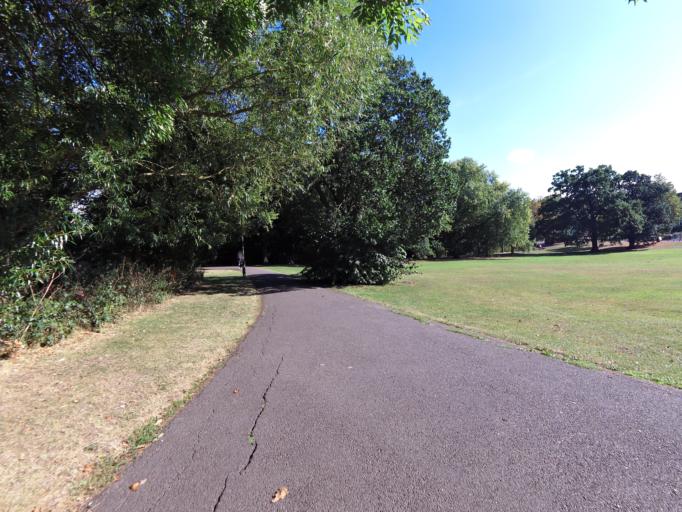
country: GB
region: England
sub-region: Greater London
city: Hadley Wood
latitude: 51.6389
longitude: -0.1590
